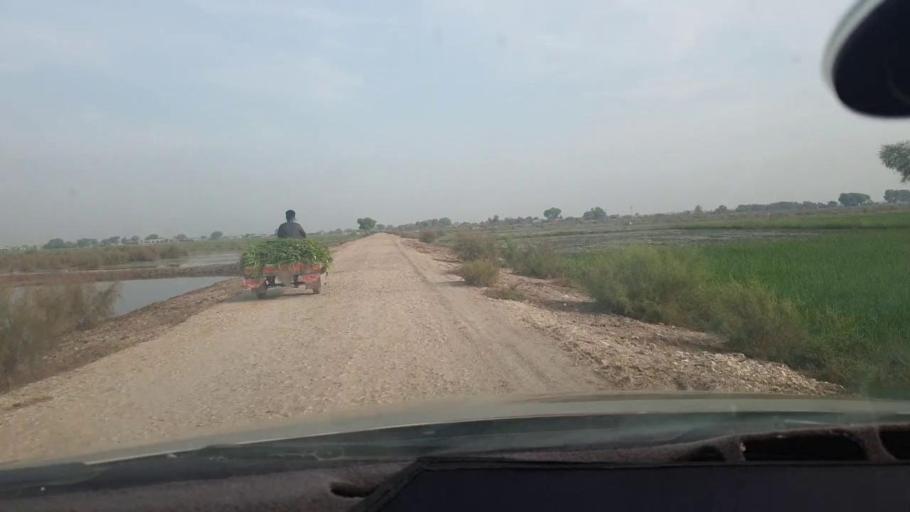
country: PK
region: Balochistan
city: Jhatpat
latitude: 28.3630
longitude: 68.4062
